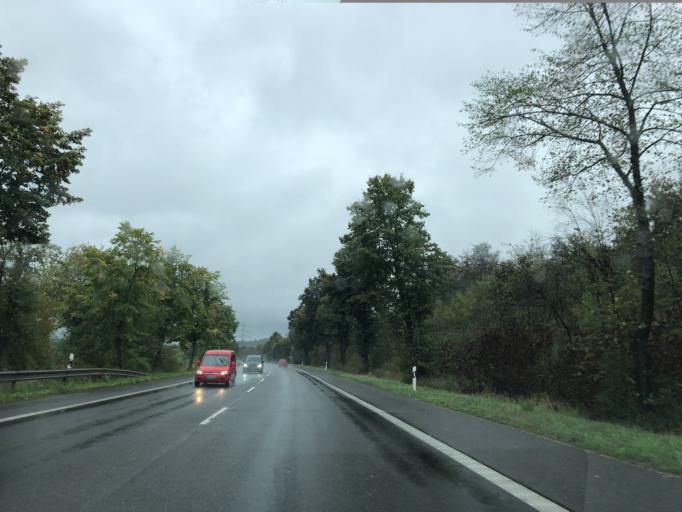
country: DE
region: North Rhine-Westphalia
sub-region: Regierungsbezirk Dusseldorf
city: Grevenbroich
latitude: 51.0685
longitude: 6.5570
